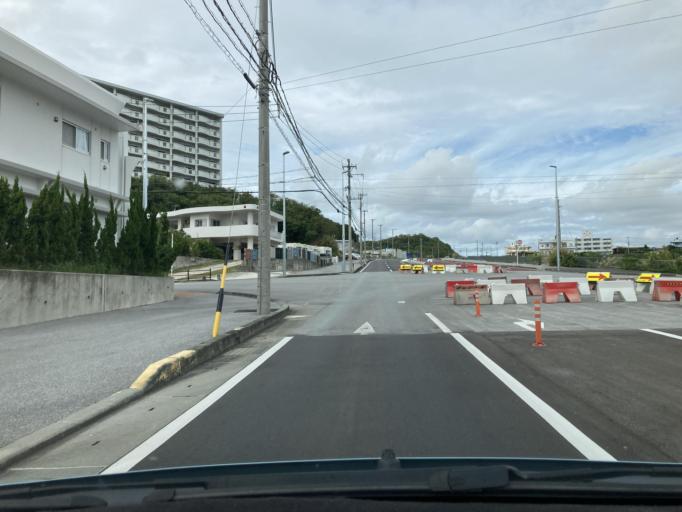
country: JP
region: Okinawa
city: Tomigusuku
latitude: 26.1657
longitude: 127.6782
